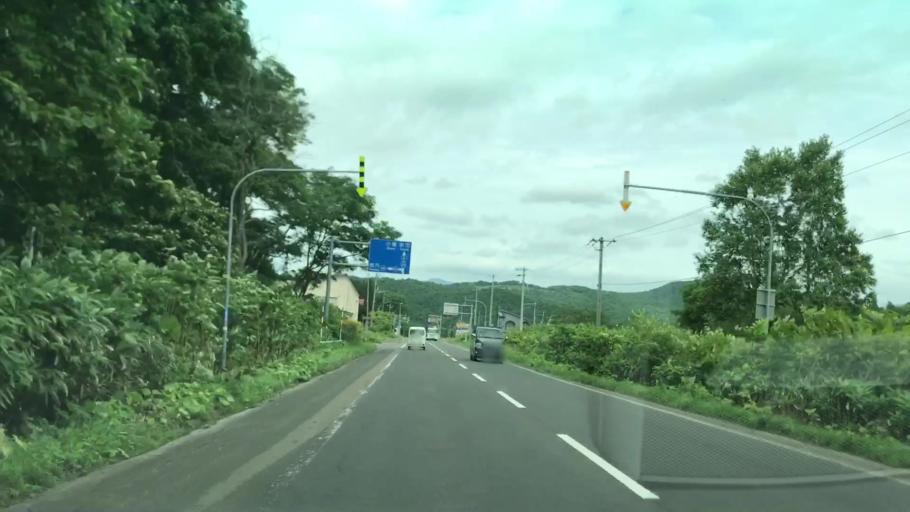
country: JP
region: Hokkaido
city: Niseko Town
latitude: 42.9571
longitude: 140.6958
